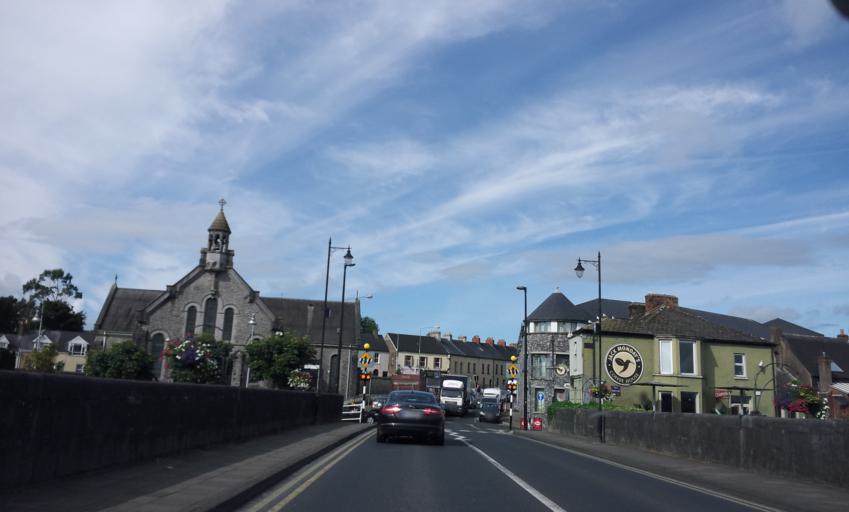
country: IE
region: Munster
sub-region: County Limerick
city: Luimneach
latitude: 52.6700
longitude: -8.6276
